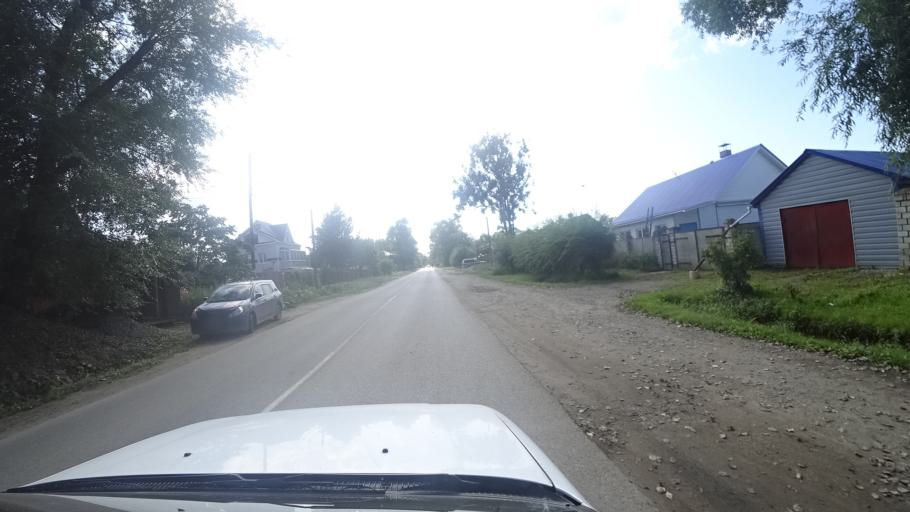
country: RU
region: Primorskiy
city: Dal'nerechensk
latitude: 45.9288
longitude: 133.7358
